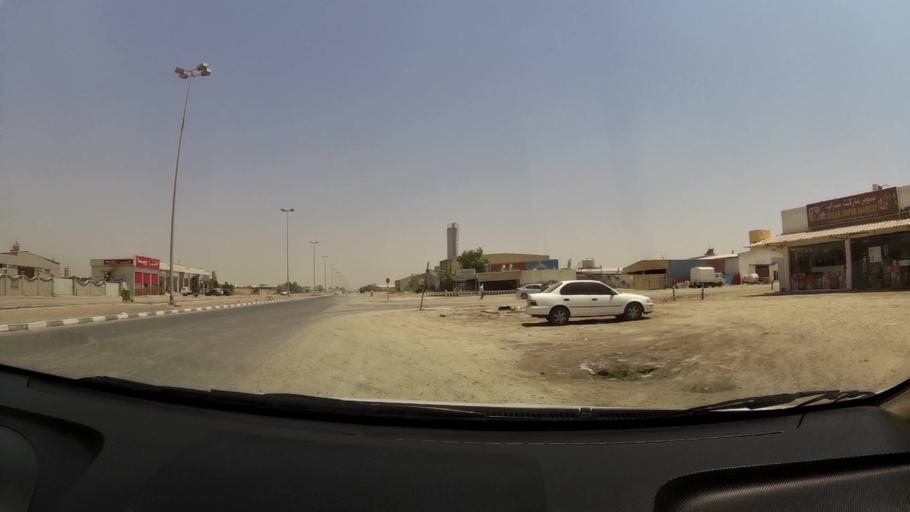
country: AE
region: Umm al Qaywayn
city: Umm al Qaywayn
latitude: 25.5090
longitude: 55.5588
